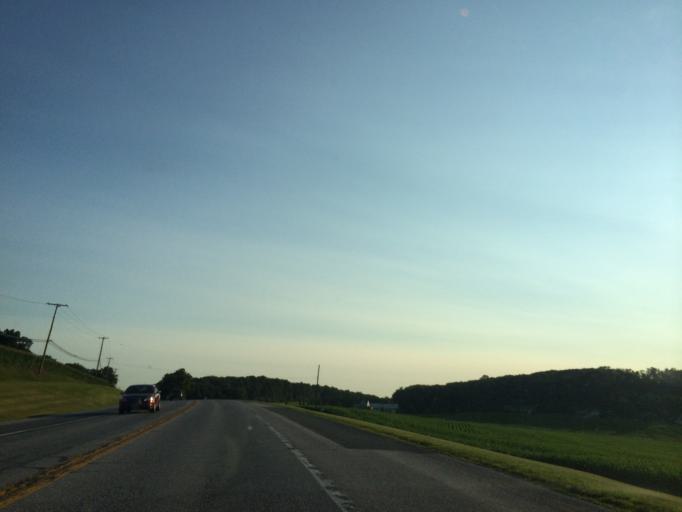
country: US
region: Maryland
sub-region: Carroll County
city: Manchester
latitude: 39.6234
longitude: -76.9341
